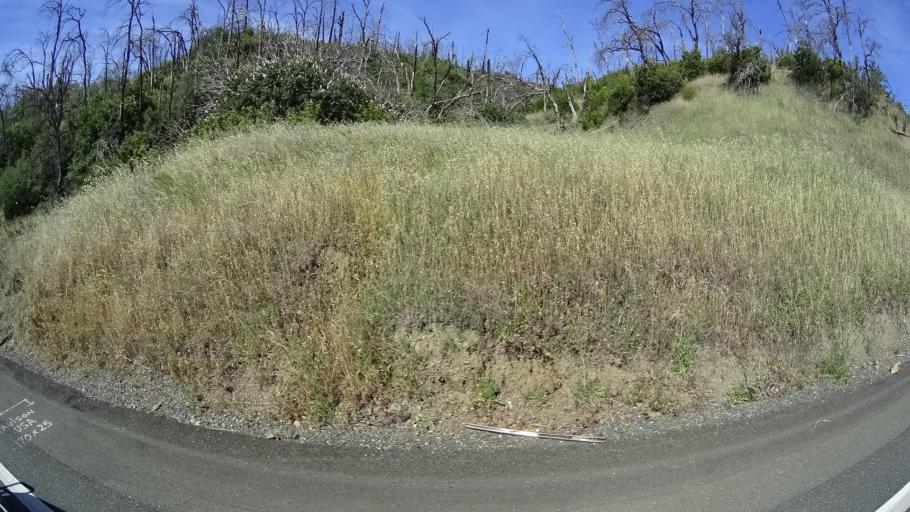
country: US
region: California
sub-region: Lake County
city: Cobb
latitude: 38.7859
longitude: -122.6925
